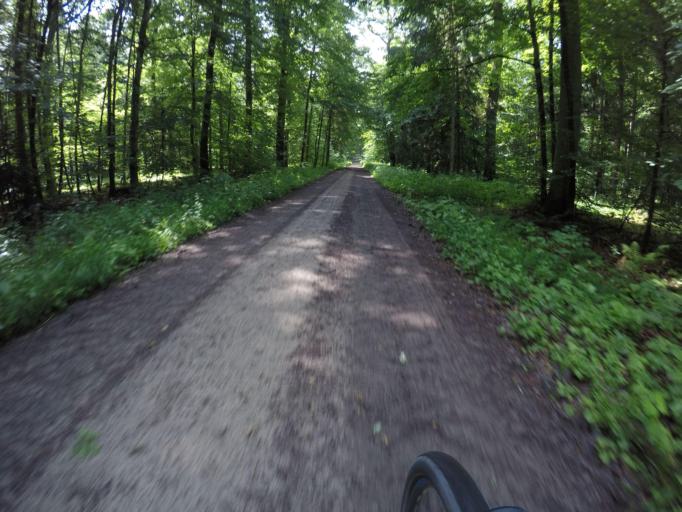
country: DE
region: Baden-Wuerttemberg
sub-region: Regierungsbezirk Stuttgart
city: Nufringen
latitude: 48.6403
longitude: 8.8601
